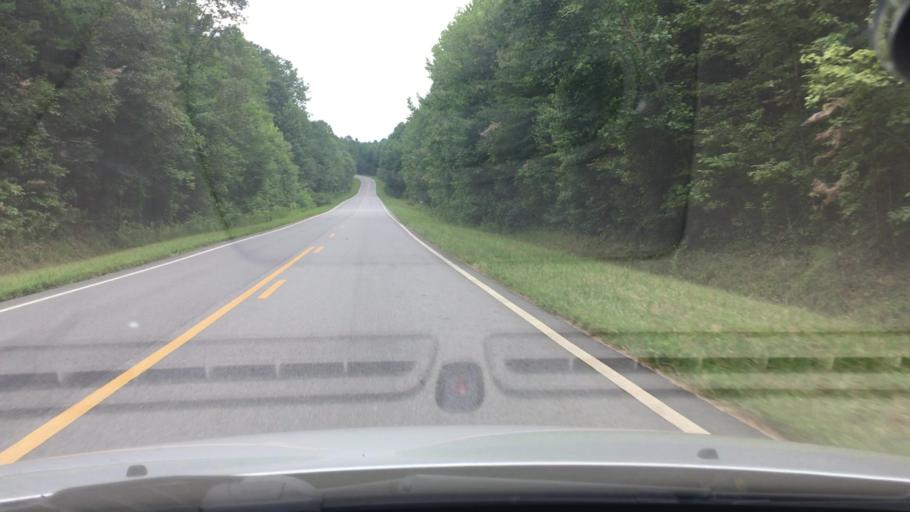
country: US
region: Georgia
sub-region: Lumpkin County
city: Dahlonega
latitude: 34.6148
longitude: -83.8993
